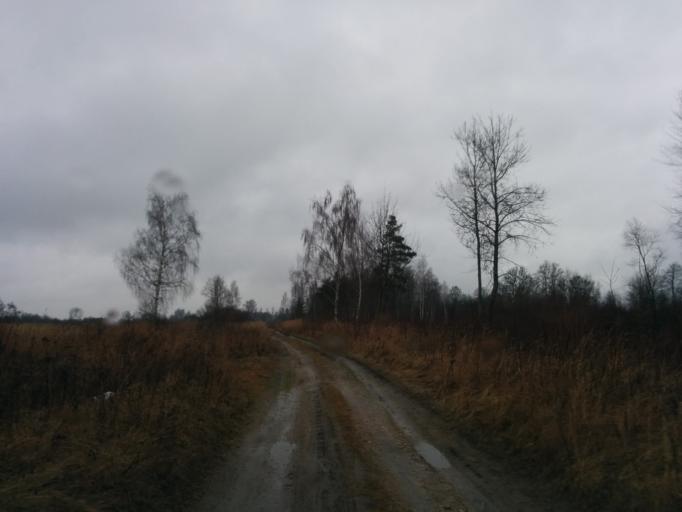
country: LV
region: Jelgava
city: Jelgava
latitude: 56.6764
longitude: 23.7106
